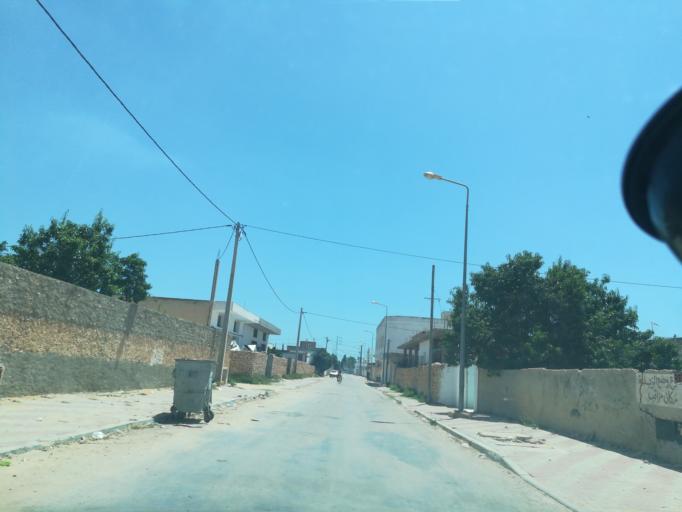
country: TN
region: Safaqis
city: Al Qarmadah
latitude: 34.8234
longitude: 10.7549
